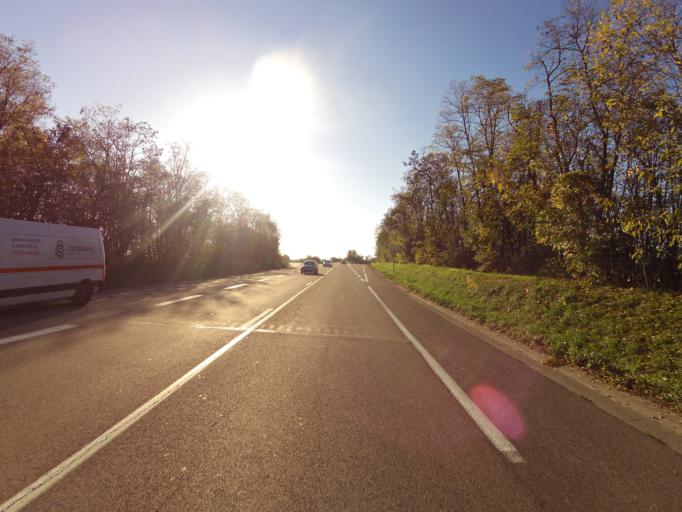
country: FR
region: Champagne-Ardenne
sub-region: Departement de l'Aube
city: Bucheres
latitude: 48.2354
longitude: 4.1228
